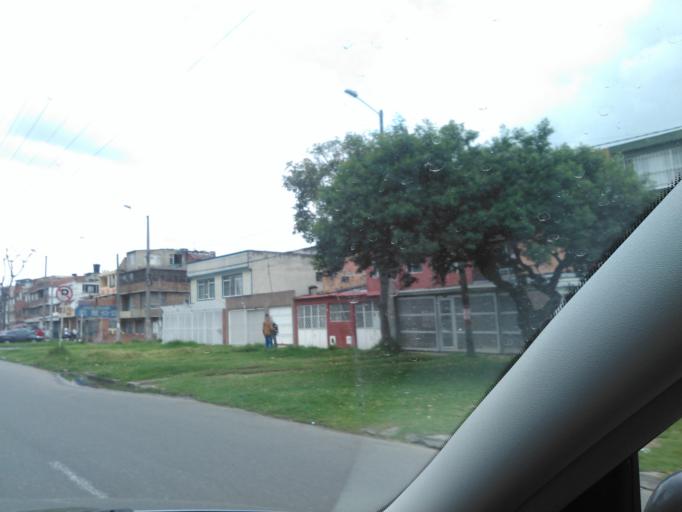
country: CO
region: Bogota D.C.
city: Bogota
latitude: 4.6171
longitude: -74.1098
